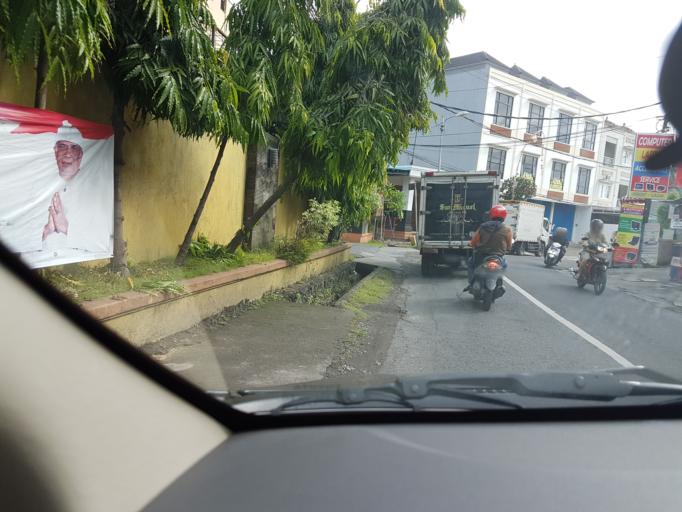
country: ID
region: Bali
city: Denpasar
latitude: -8.6644
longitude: 115.1932
